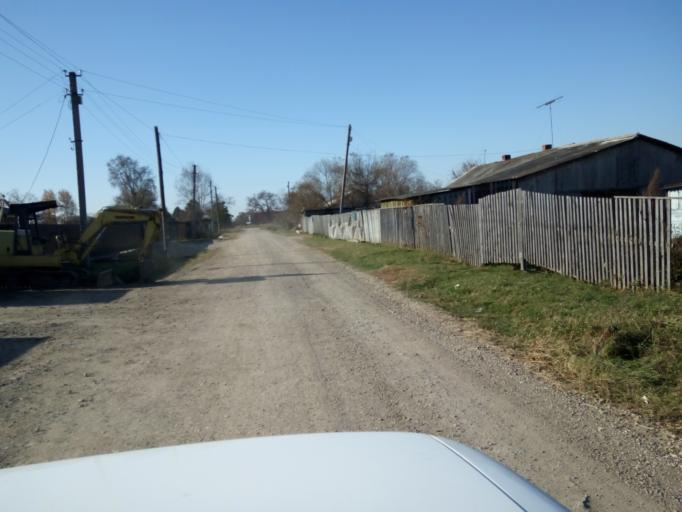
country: RU
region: Primorskiy
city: Lazo
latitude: 45.8741
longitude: 133.6548
